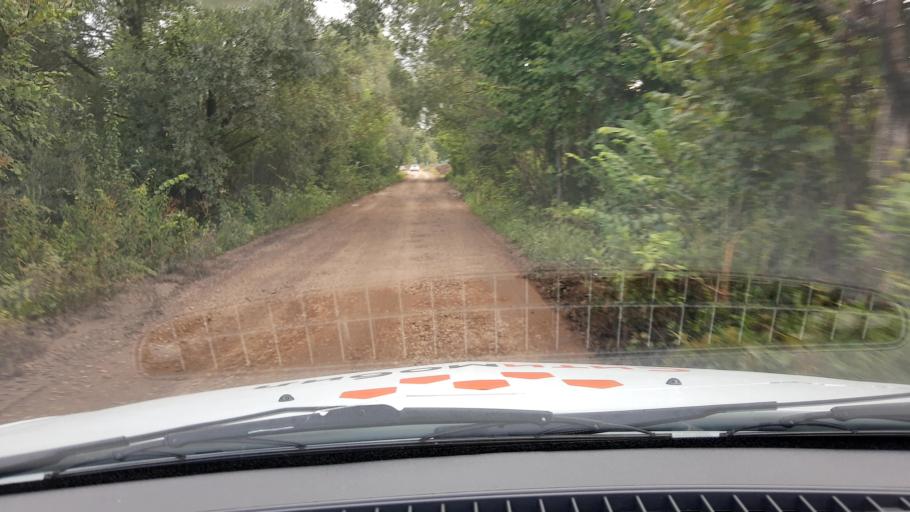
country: RU
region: Bashkortostan
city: Kabakovo
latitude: 54.6998
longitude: 56.1344
